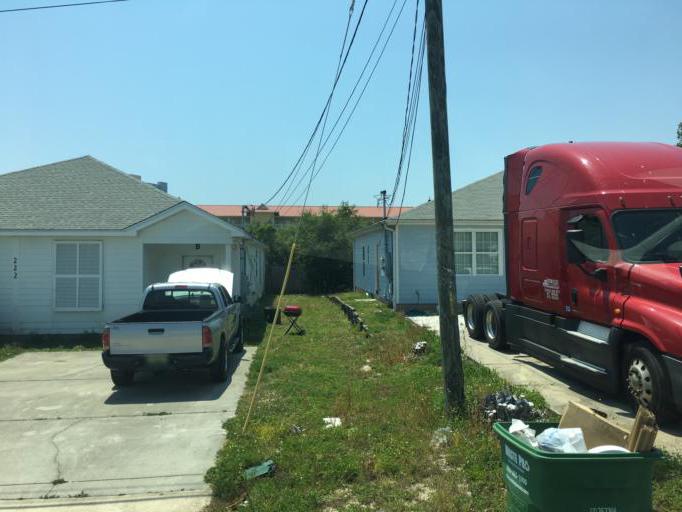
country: US
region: Florida
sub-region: Bay County
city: Laguna Beach
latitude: 30.2261
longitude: -85.8907
